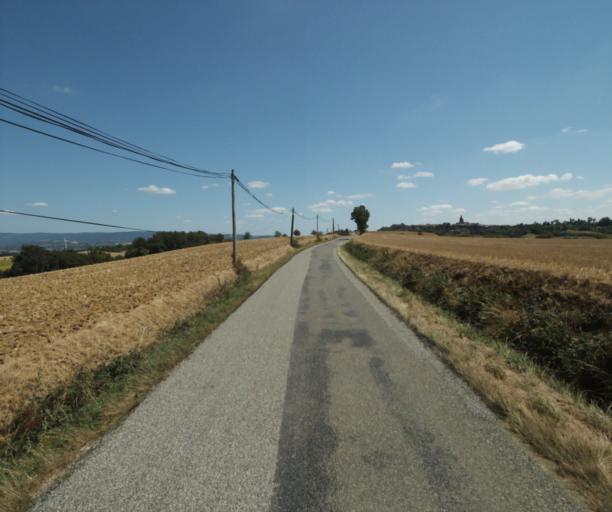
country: FR
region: Midi-Pyrenees
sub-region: Departement de la Haute-Garonne
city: Saint-Felix-Lauragais
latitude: 43.4602
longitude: 1.8804
